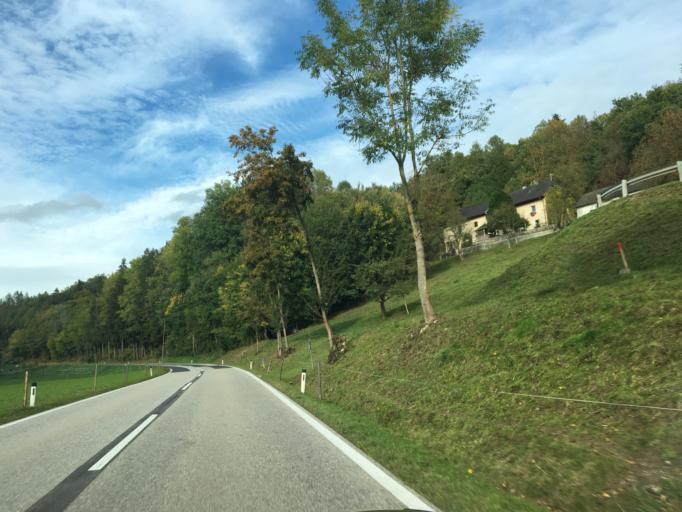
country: AT
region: Upper Austria
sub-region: Politischer Bezirk Urfahr-Umgebung
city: Feldkirchen an der Donau
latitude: 48.3697
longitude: 14.0634
